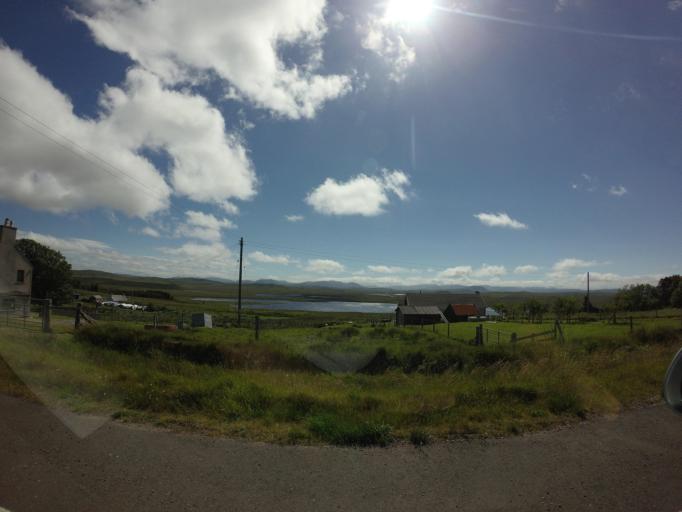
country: GB
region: Scotland
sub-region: Eilean Siar
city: Stornoway
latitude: 58.1714
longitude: -6.5716
